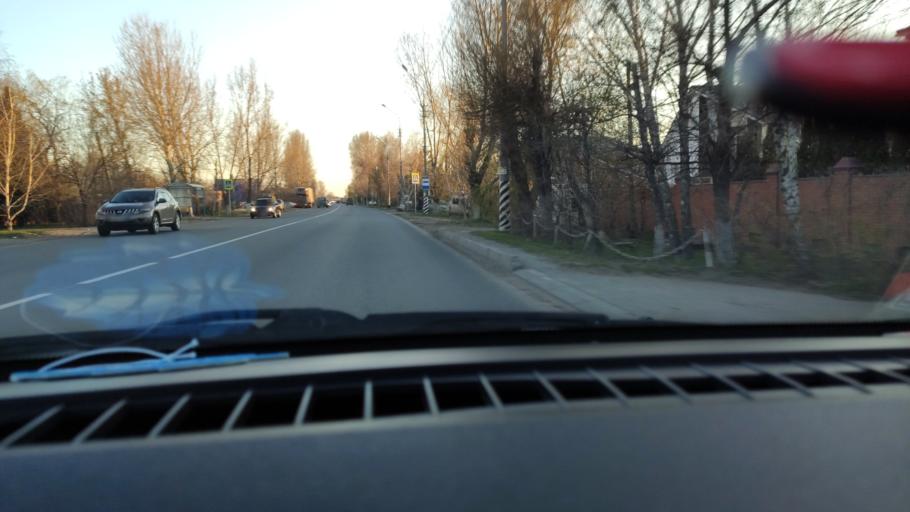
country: RU
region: Saratov
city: Privolzhskiy
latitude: 51.4320
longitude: 46.0560
